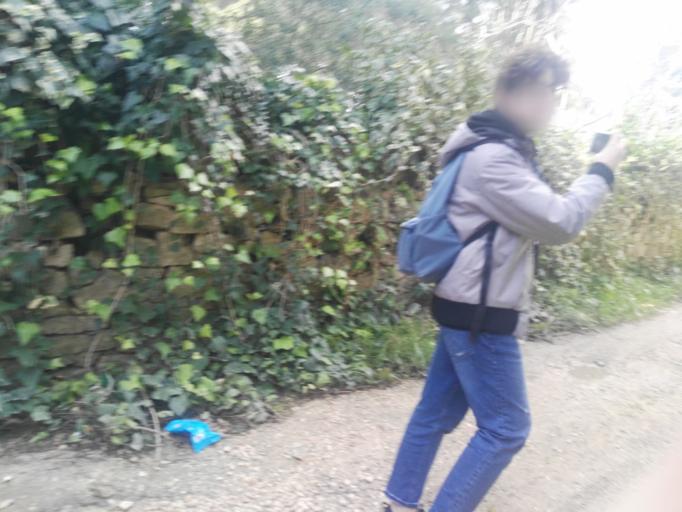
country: IT
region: Apulia
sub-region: Provincia di Barletta - Andria - Trani
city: Andria
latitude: 41.2177
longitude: 16.3078
